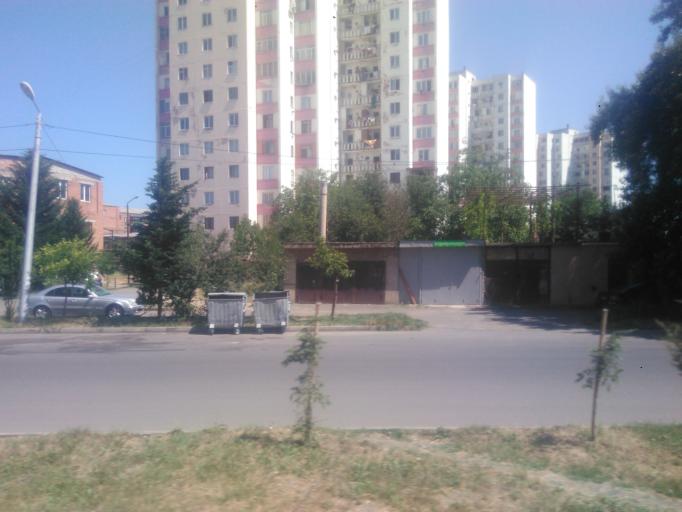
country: GE
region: T'bilisi
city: Tbilisi
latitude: 41.7077
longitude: 44.8829
